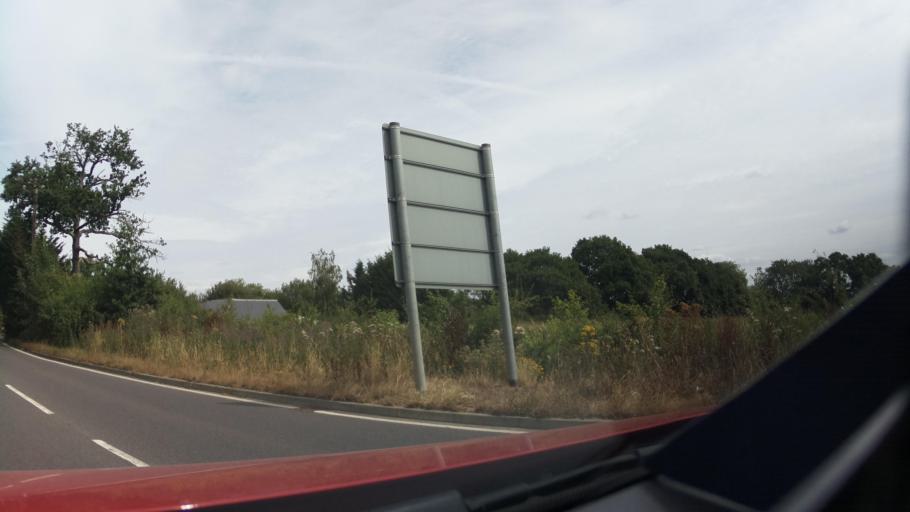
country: GB
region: England
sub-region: Surrey
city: Salfords
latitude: 51.1899
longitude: -0.1964
